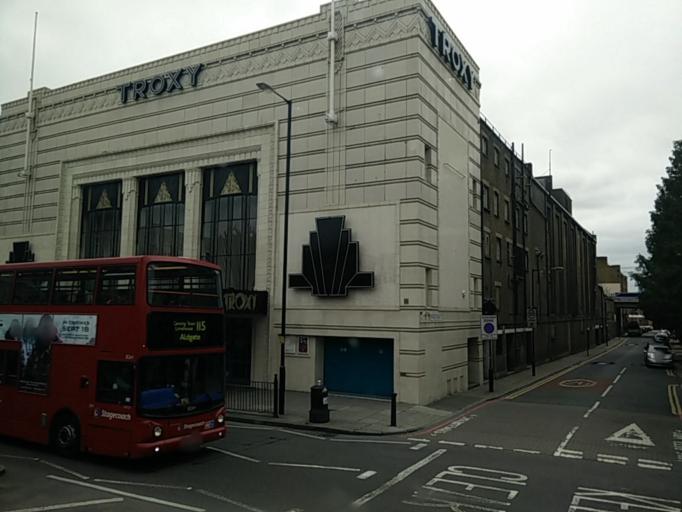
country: GB
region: England
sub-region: Greater London
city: Bethnal Green
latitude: 51.5132
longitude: -0.0444
